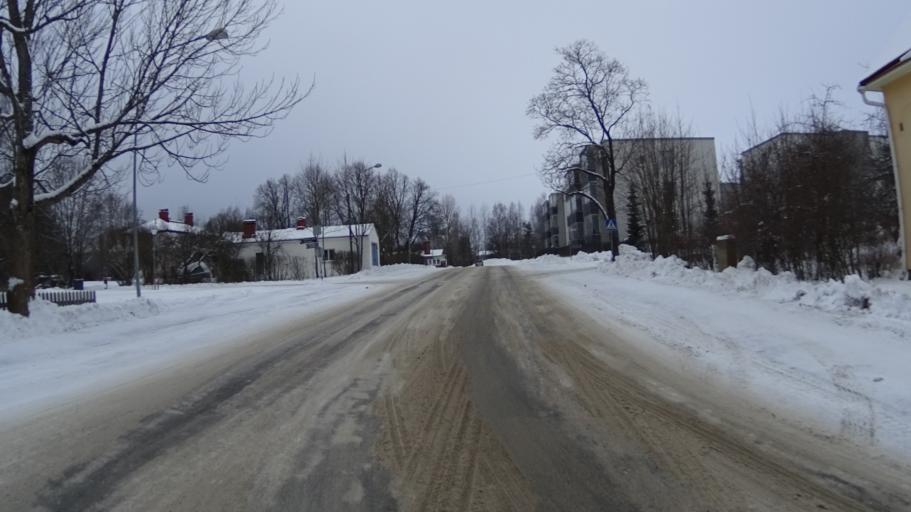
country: FI
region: Uusimaa
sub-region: Helsinki
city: Karkkila
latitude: 60.5328
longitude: 24.2080
